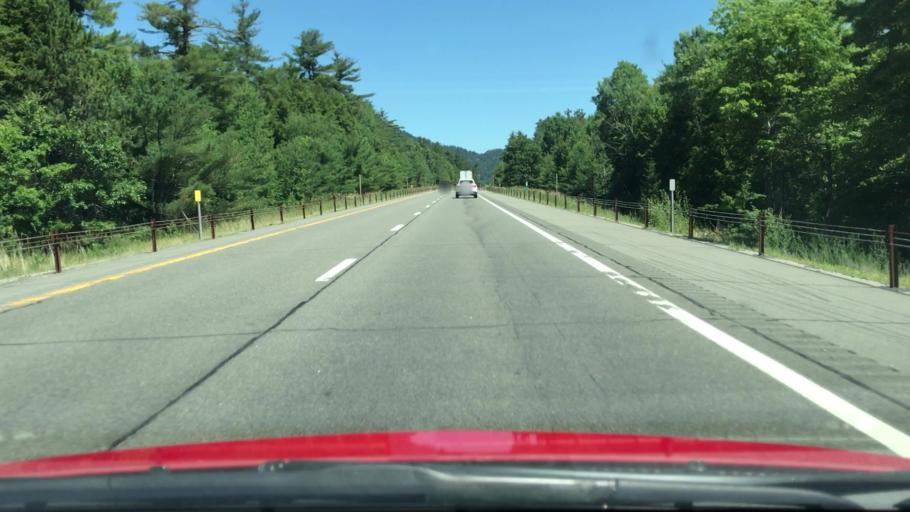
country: US
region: New York
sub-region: Essex County
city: Mineville
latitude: 43.9731
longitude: -73.7253
